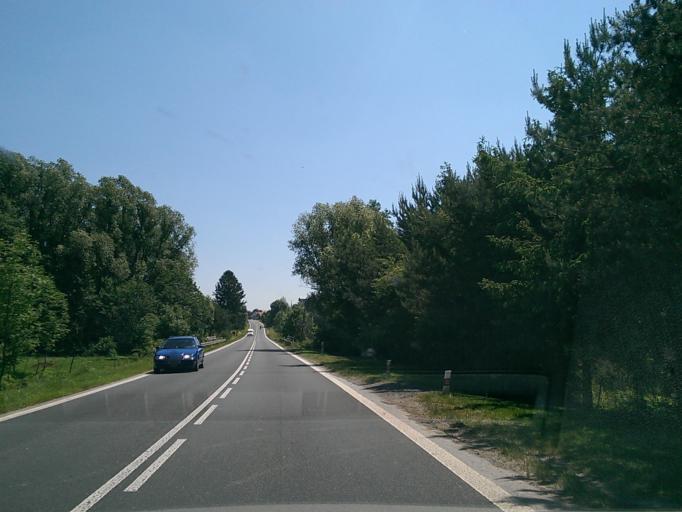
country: CZ
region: Liberecky
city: Rovensko pod Troskami
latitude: 50.5030
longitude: 15.2856
